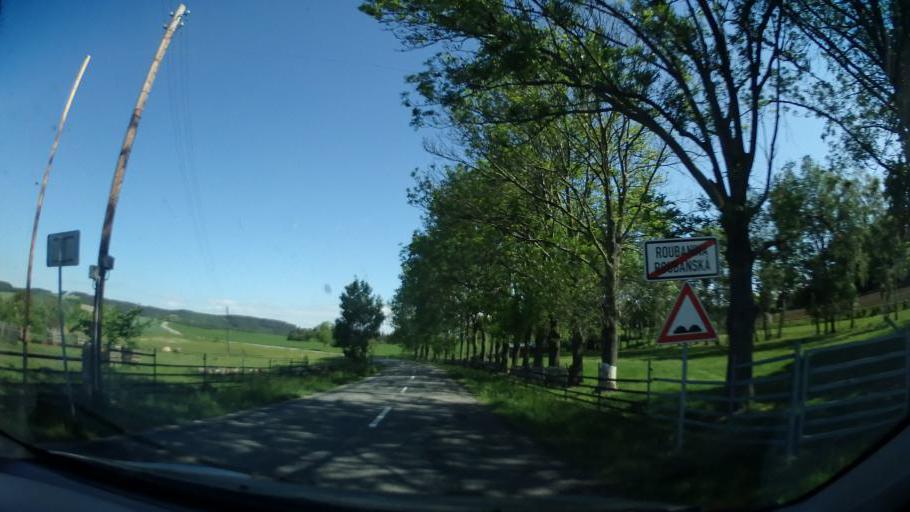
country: CZ
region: South Moravian
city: Velke Opatovice
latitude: 49.6154
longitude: 16.6090
